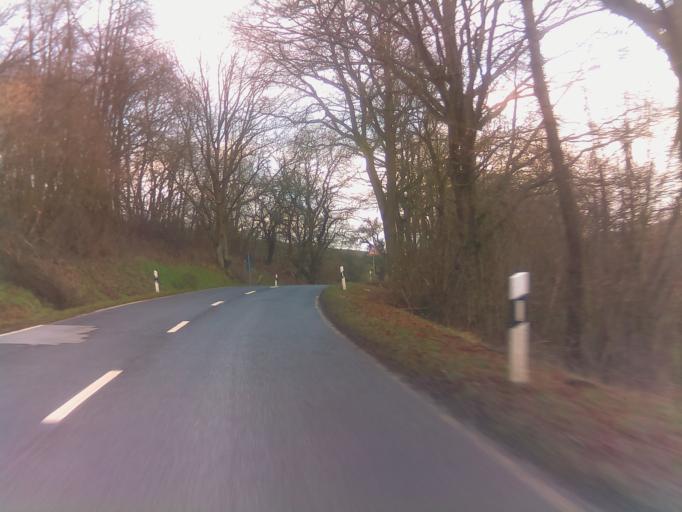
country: DE
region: Rheinland-Pfalz
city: Furfeld
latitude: 49.7745
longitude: 7.9202
